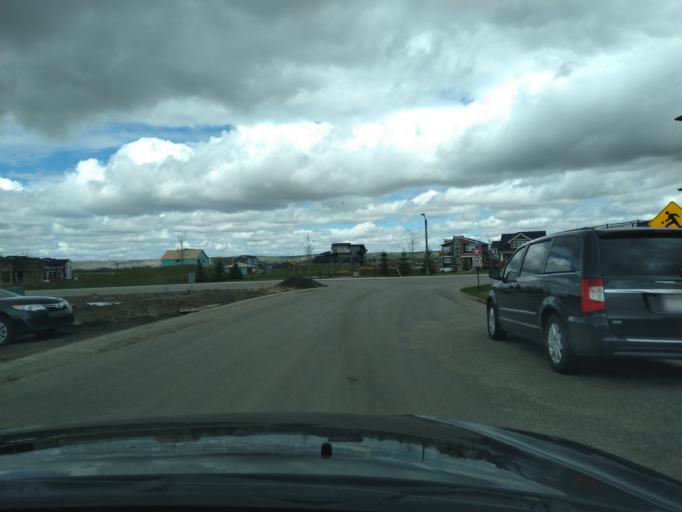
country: CA
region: Alberta
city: Cochrane
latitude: 51.1108
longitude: -114.3957
